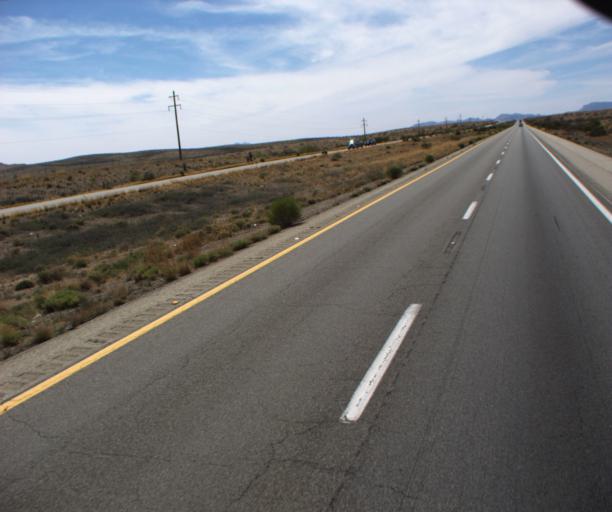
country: US
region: Arizona
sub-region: Cochise County
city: Willcox
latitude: 32.3523
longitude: -109.7235
